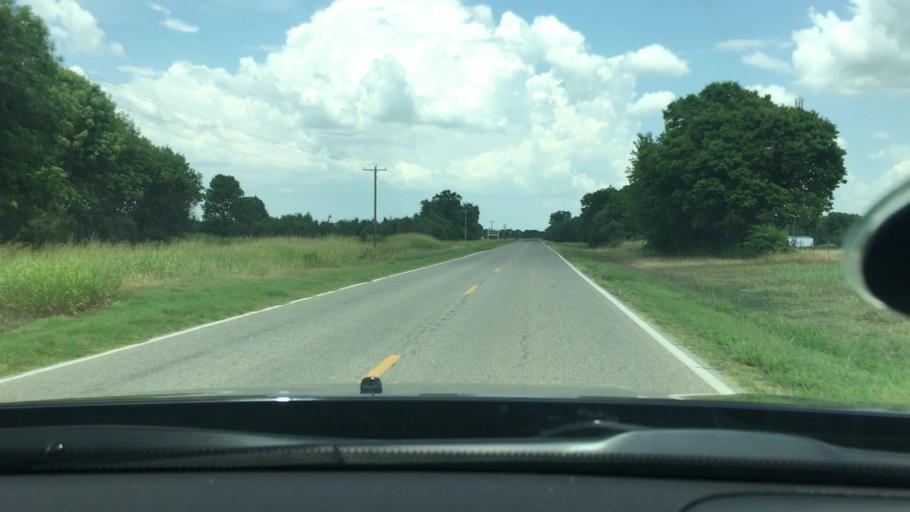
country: US
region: Oklahoma
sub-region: Marshall County
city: Oakland
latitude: 34.0100
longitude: -96.8792
